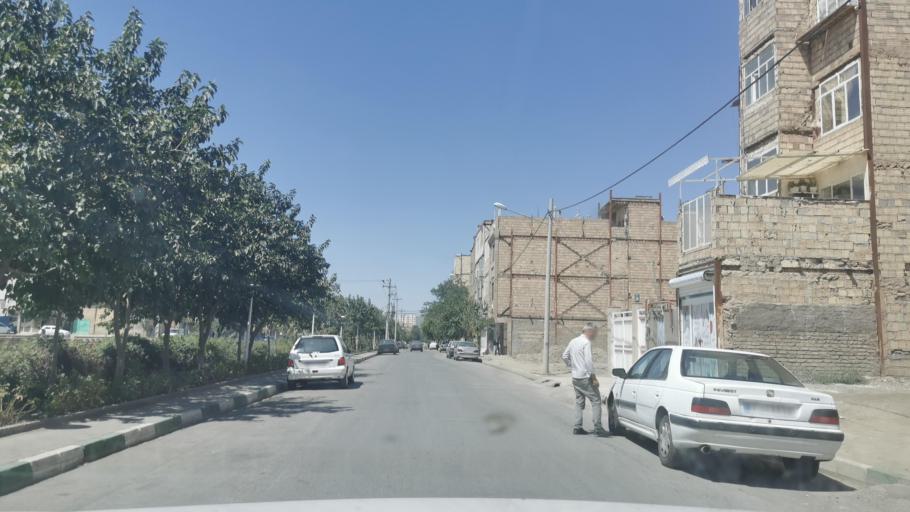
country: IR
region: Razavi Khorasan
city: Mashhad
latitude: 36.3587
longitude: 59.5626
